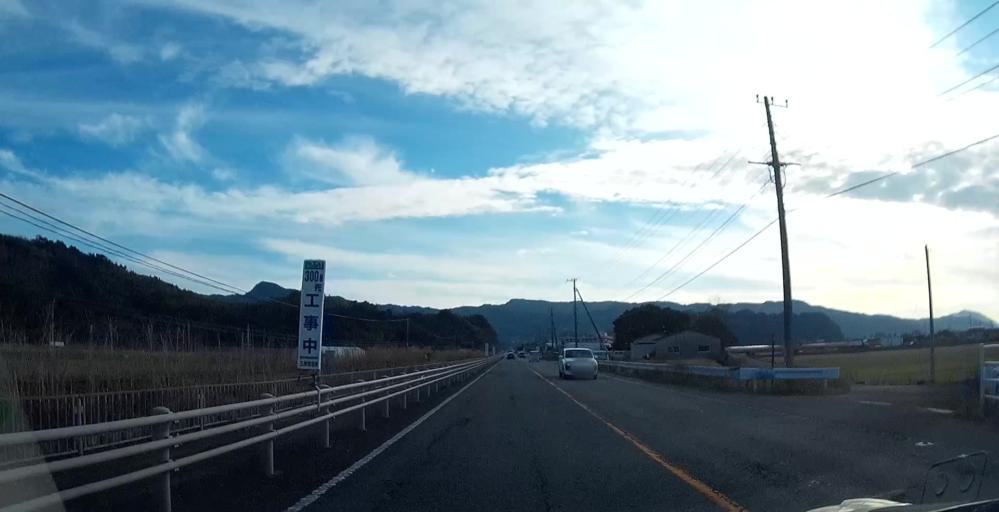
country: JP
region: Kumamoto
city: Uto
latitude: 32.6845
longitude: 130.5543
